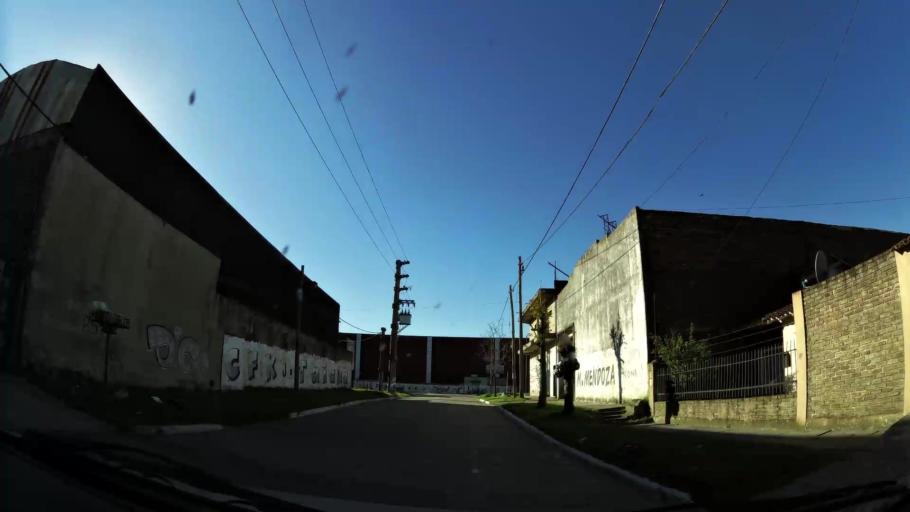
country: AR
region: Buenos Aires
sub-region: Partido de Quilmes
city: Quilmes
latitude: -34.7412
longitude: -58.3208
